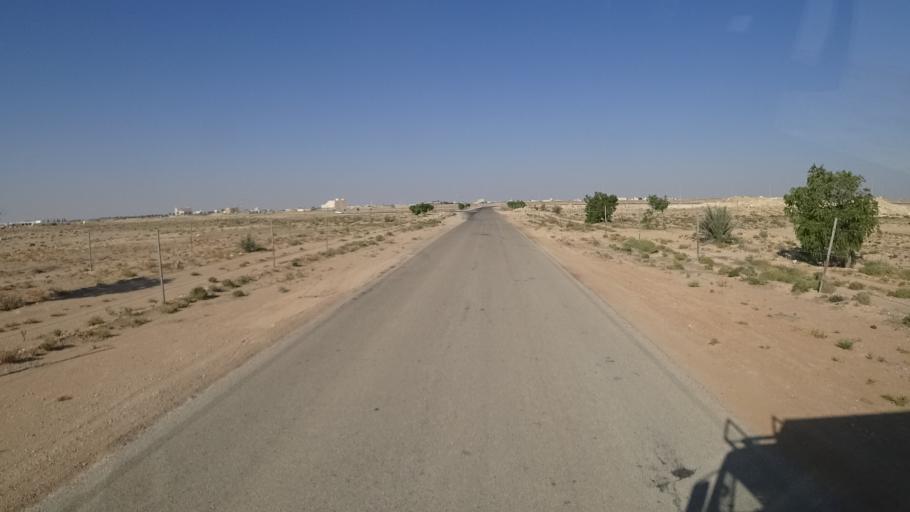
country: OM
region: Zufar
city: Salalah
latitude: 17.5972
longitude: 54.0345
